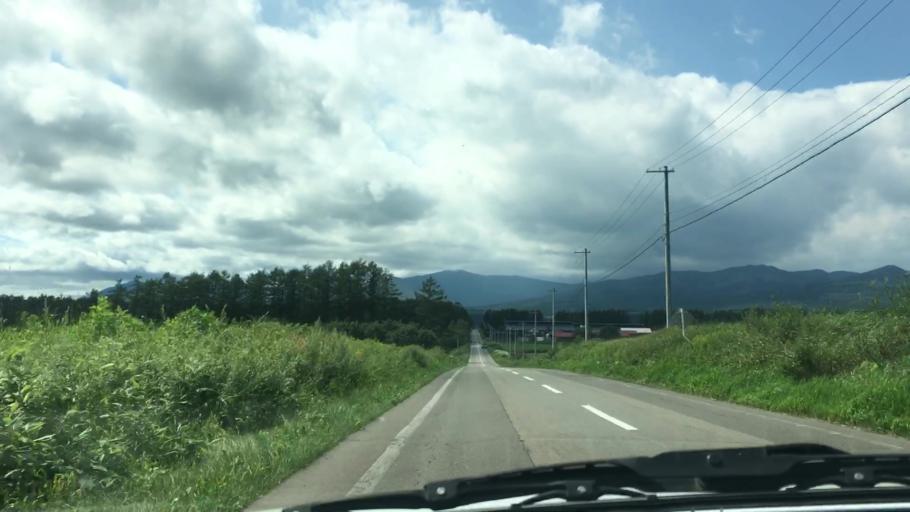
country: JP
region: Hokkaido
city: Otofuke
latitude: 43.2802
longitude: 143.3399
